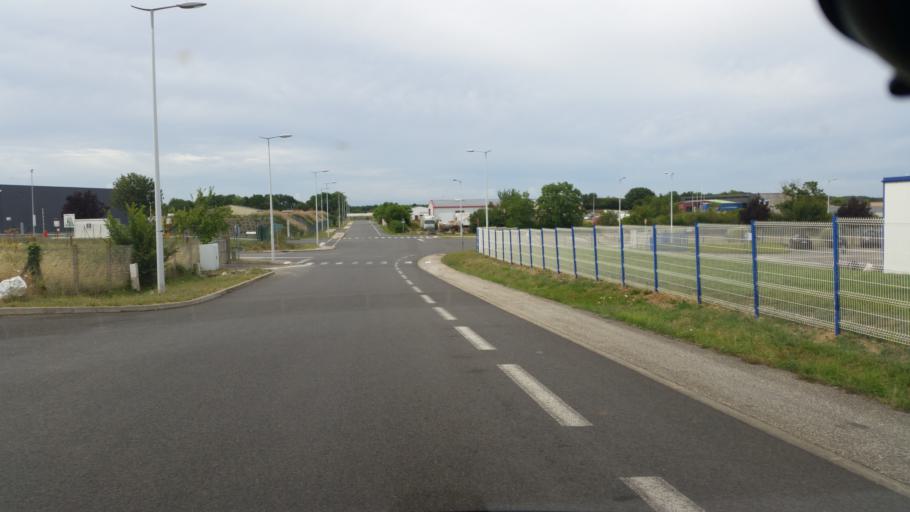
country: FR
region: Poitou-Charentes
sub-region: Departement de la Charente-Maritime
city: Surgeres
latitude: 46.1091
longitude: -0.7793
